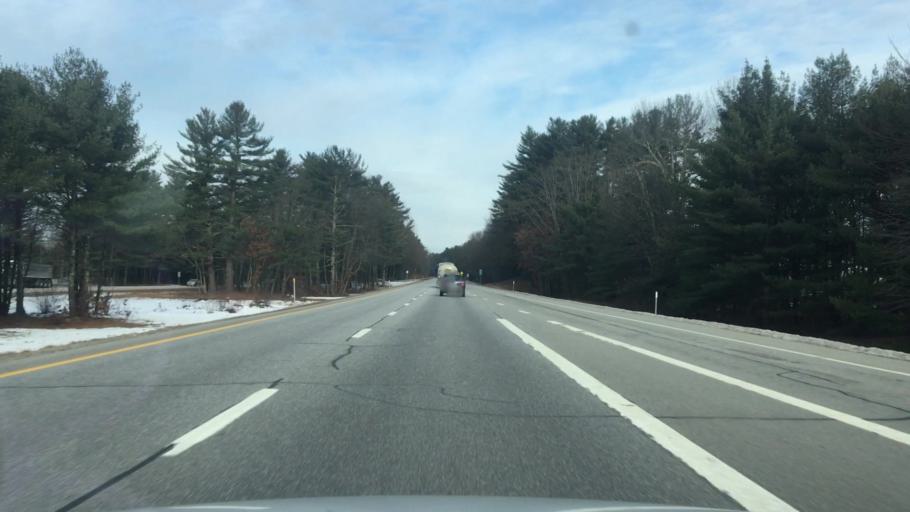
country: US
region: New Hampshire
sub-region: Merrimack County
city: Contoocook
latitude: 43.2061
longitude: -71.7102
